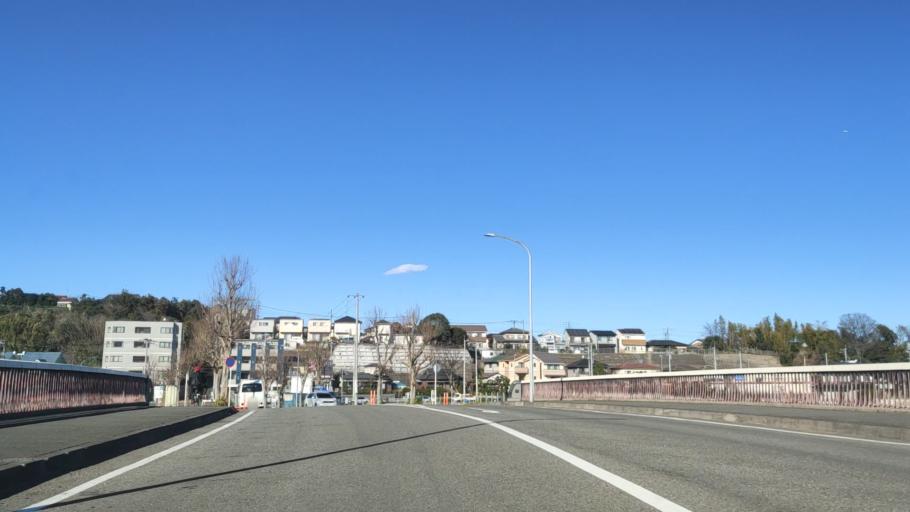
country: JP
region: Tokyo
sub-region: Machida-shi
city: Machida
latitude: 35.5171
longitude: 139.5416
